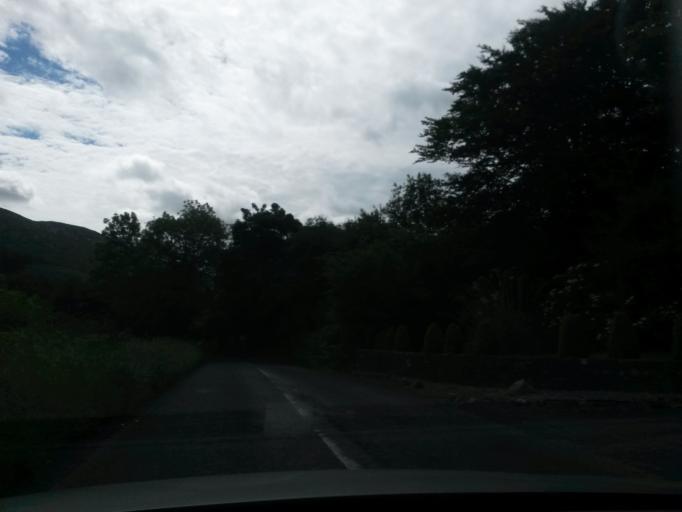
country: IE
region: Connaught
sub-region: Sligo
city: Sligo
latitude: 54.2368
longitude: -8.4085
